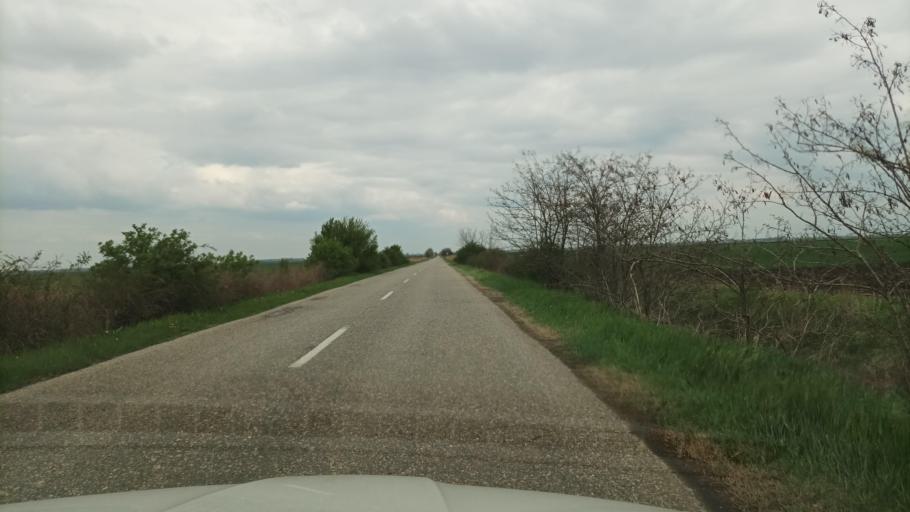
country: HU
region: Pest
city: Tortel
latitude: 47.1457
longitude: 19.9597
